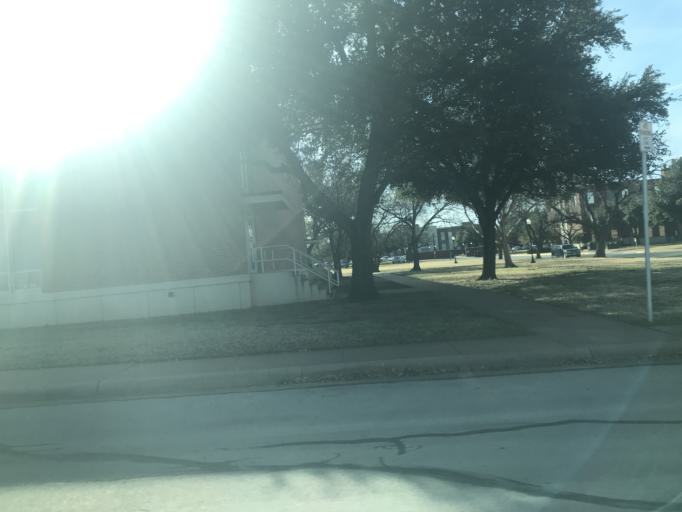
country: US
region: Texas
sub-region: Taylor County
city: Abilene
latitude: 32.4788
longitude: -99.7345
